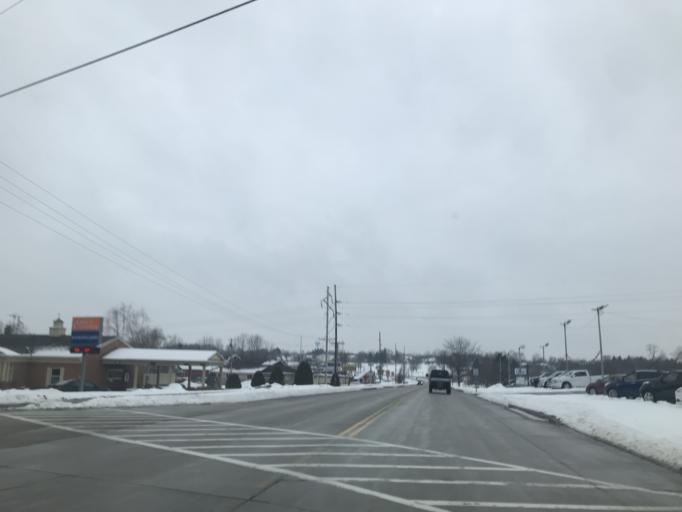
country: US
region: Wisconsin
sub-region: Door County
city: Sturgeon Bay
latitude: 44.8238
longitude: -87.3872
